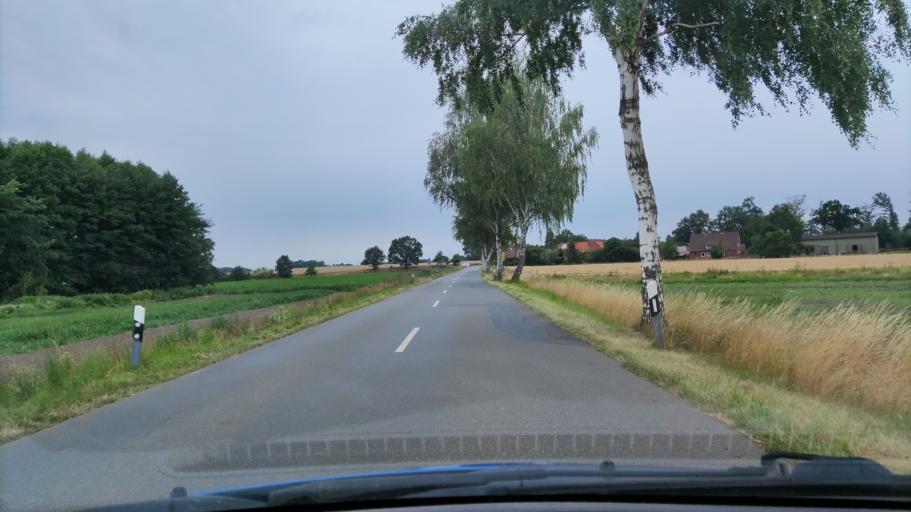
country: DE
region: Lower Saxony
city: Rosche
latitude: 52.9736
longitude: 10.7893
